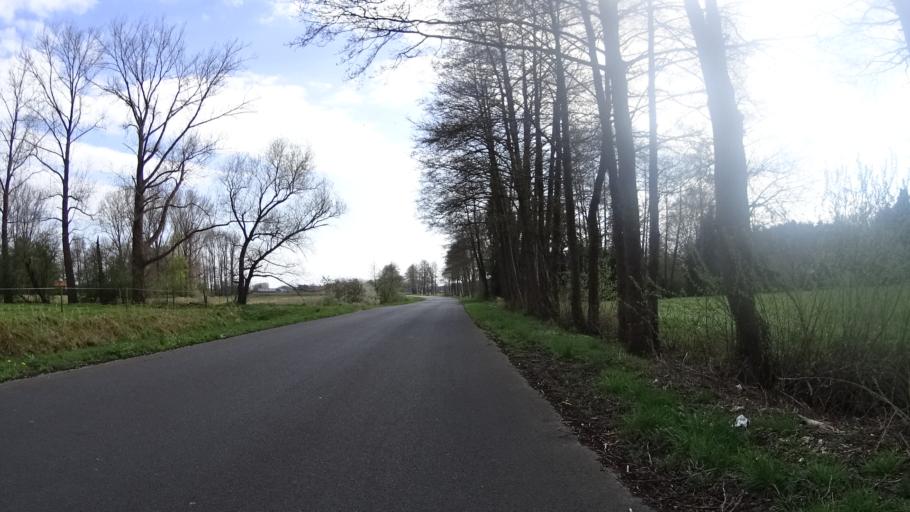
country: DE
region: Lower Saxony
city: Lehe
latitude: 53.0382
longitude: 7.3221
